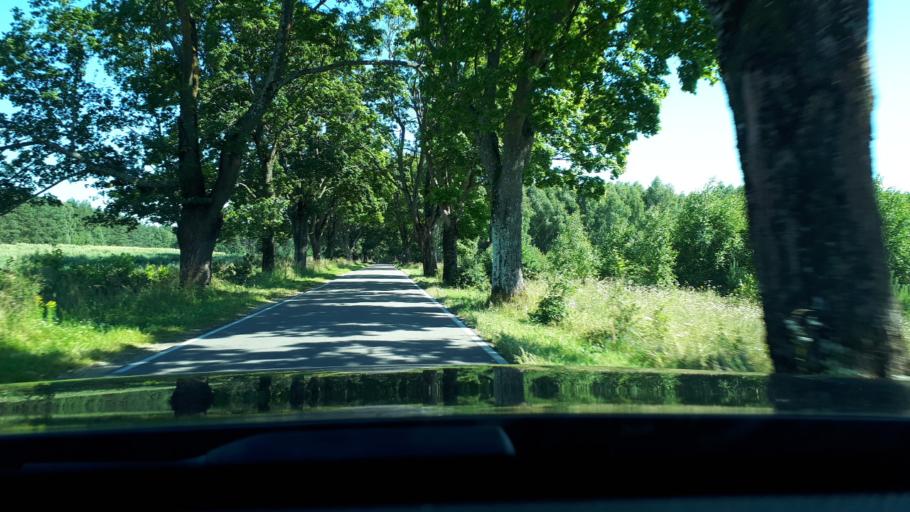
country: PL
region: Warmian-Masurian Voivodeship
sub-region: Powiat olsztynski
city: Stawiguda
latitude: 53.5939
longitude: 20.4290
